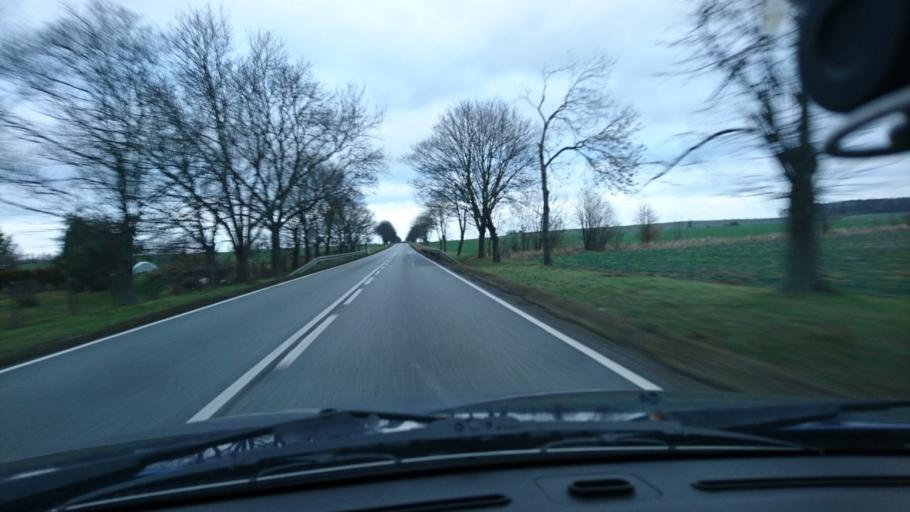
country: PL
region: Opole Voivodeship
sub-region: Powiat kluczborski
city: Byczyna
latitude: 51.0855
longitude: 18.1986
